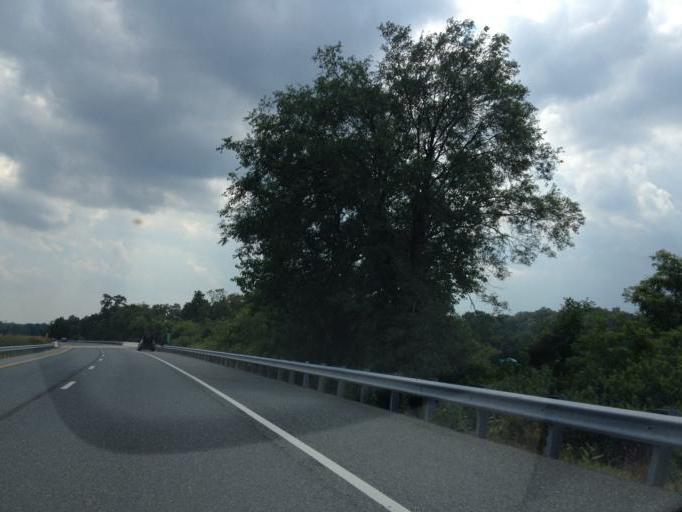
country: US
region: Maryland
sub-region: Baltimore County
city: Lansdowne
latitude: 39.2323
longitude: -76.6697
